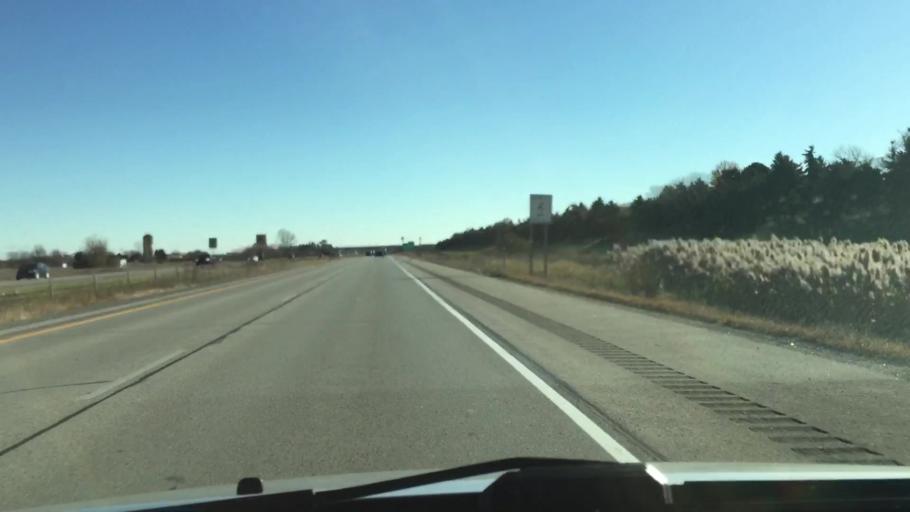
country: US
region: Wisconsin
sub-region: Outagamie County
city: Kimberly
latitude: 44.2979
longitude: -88.3427
